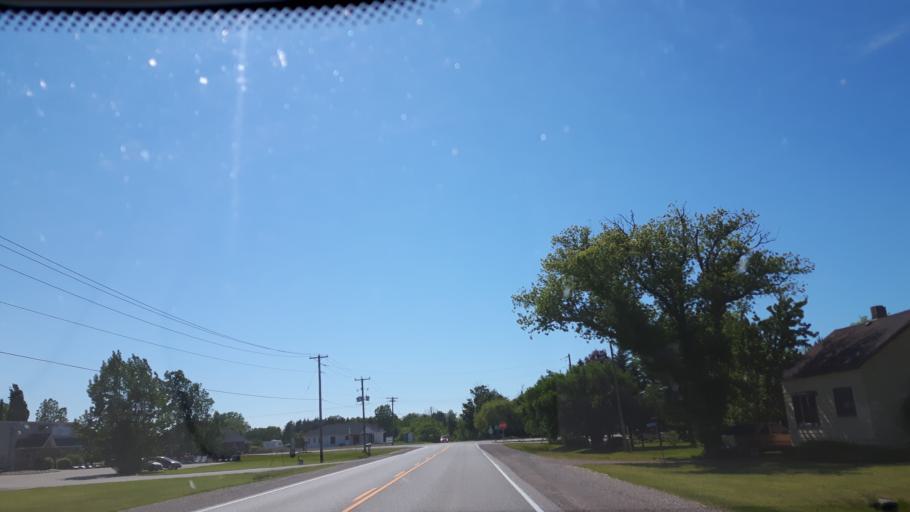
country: CA
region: Ontario
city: Bluewater
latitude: 43.4131
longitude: -81.7042
